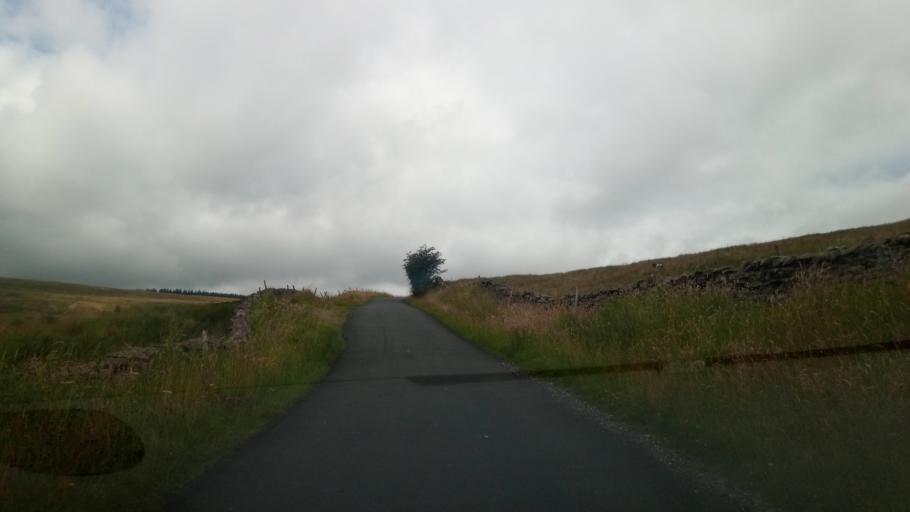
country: GB
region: England
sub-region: North Yorkshire
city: Ingleton
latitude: 54.2805
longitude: -2.3687
